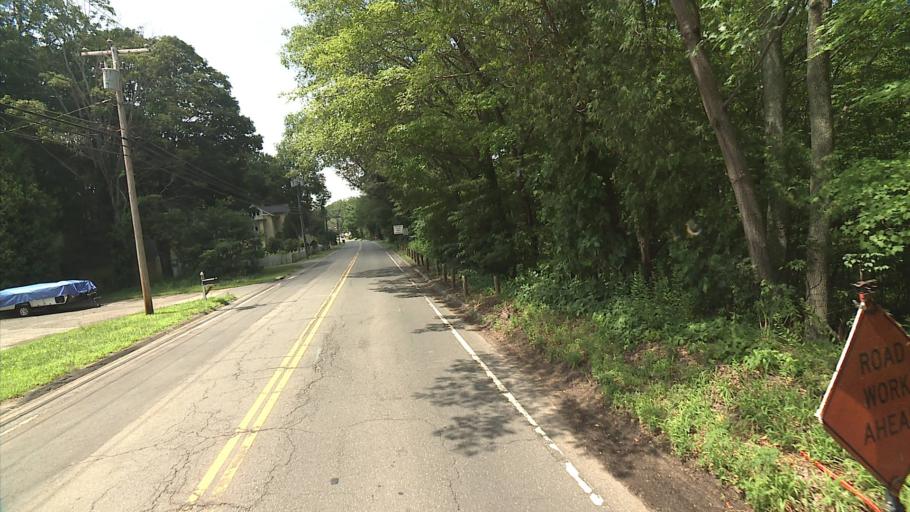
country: US
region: Connecticut
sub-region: Tolland County
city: South Coventry
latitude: 41.7655
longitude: -72.2904
